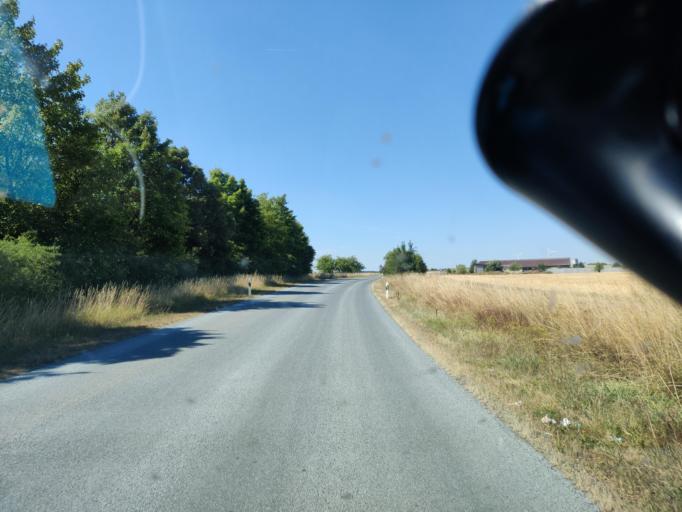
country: DE
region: Bavaria
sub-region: Regierungsbezirk Mittelfranken
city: Nennslingen
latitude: 49.0438
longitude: 11.1238
